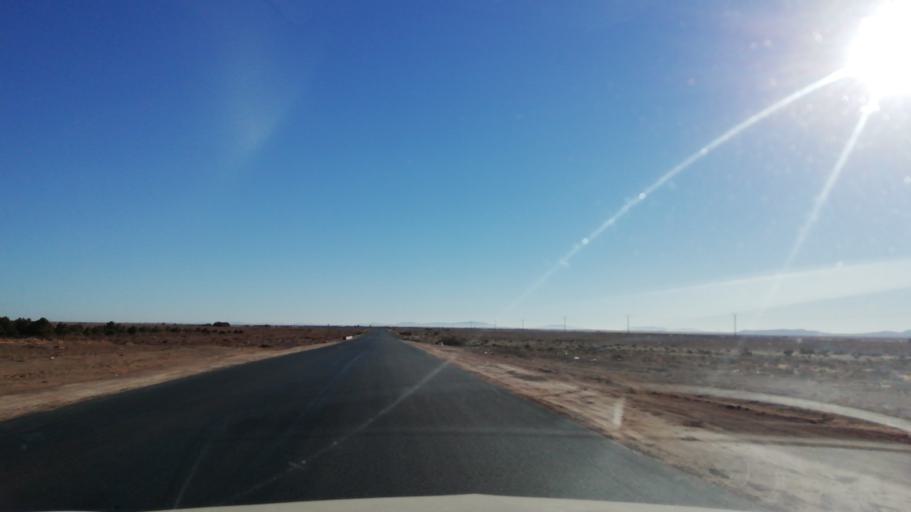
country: DZ
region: El Bayadh
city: El Bayadh
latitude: 33.8560
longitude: 0.5933
